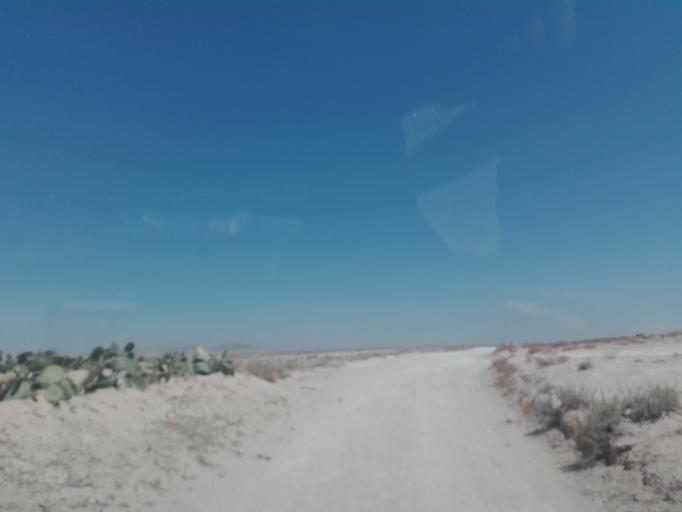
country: TN
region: Safaqis
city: Skhira
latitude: 34.3910
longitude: 9.9240
